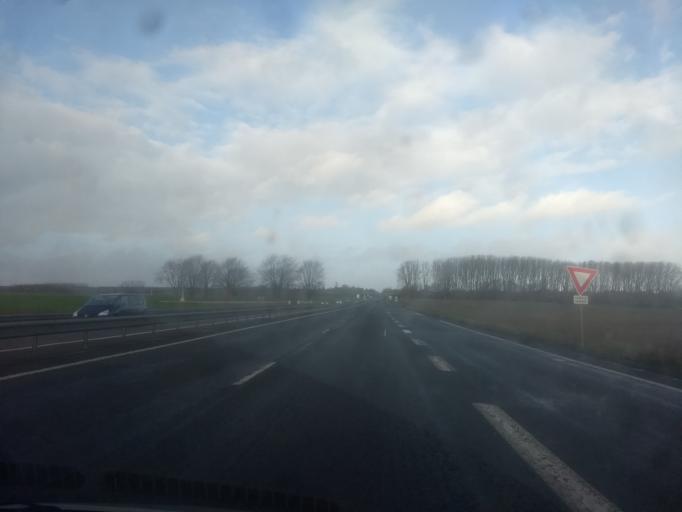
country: FR
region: Nord-Pas-de-Calais
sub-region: Departement du Pas-de-Calais
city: Thelus
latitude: 50.3448
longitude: 2.7843
